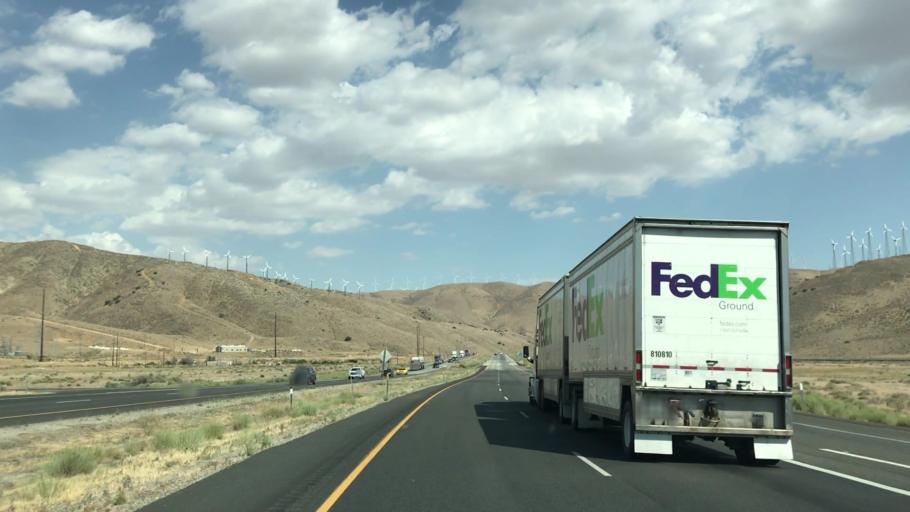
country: US
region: California
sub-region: Kern County
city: Tehachapi
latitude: 35.1091
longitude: -118.3205
